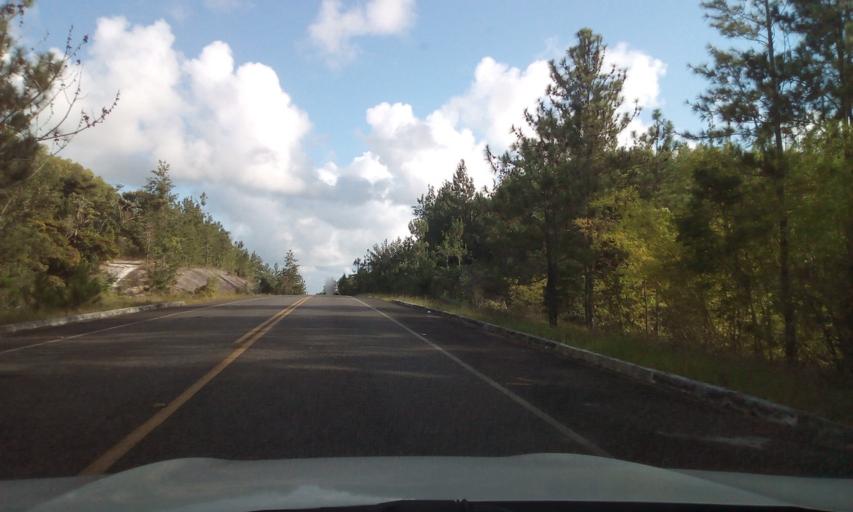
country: BR
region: Bahia
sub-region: Entre Rios
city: Entre Rios
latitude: -12.1223
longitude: -37.7891
